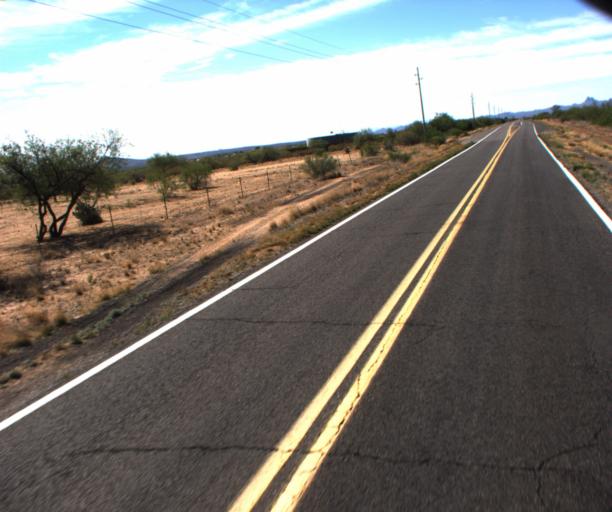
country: US
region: Arizona
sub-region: Yavapai County
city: Congress
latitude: 34.1154
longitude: -112.8346
